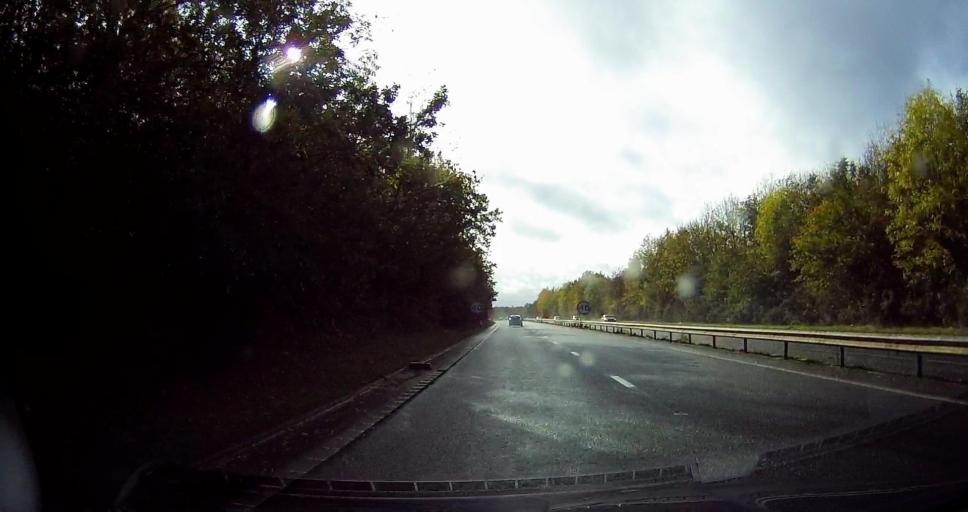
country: GB
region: England
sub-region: Warwickshire
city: Curdworth
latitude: 52.5508
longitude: -1.7754
